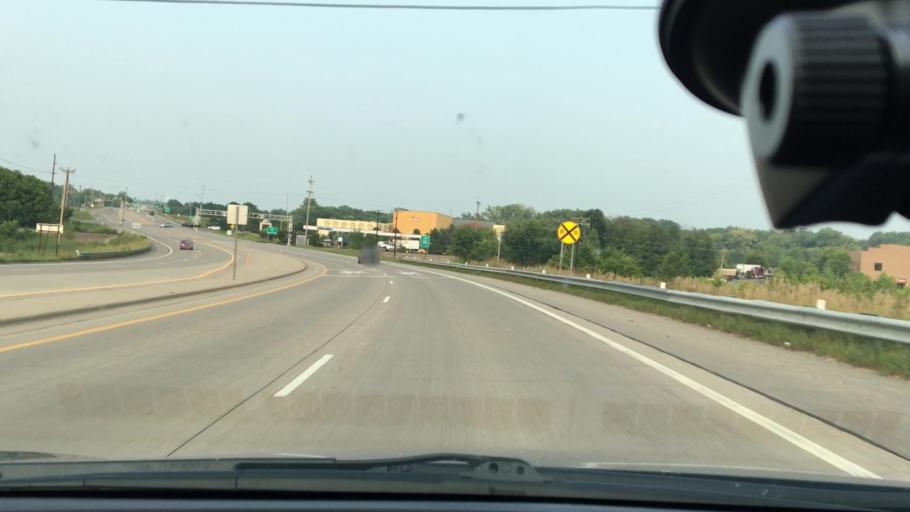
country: US
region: Minnesota
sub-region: Hennepin County
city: Rogers
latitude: 45.2149
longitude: -93.6013
